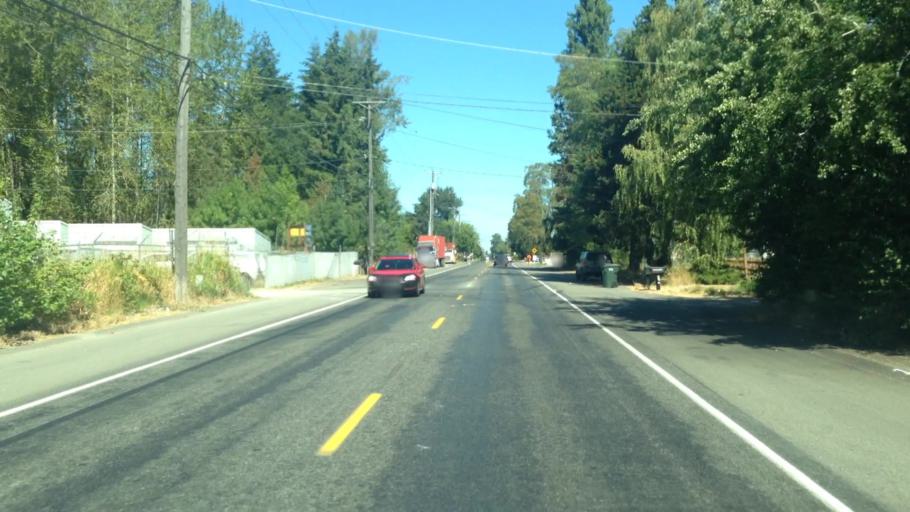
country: US
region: Washington
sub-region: Pierce County
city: Midland
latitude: 47.1599
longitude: -122.4155
